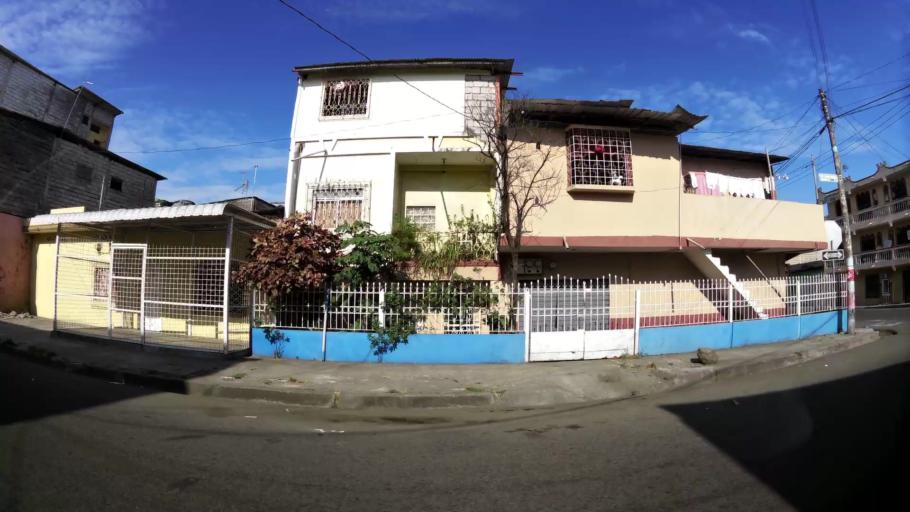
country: EC
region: Guayas
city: Guayaquil
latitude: -2.2152
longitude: -79.9272
